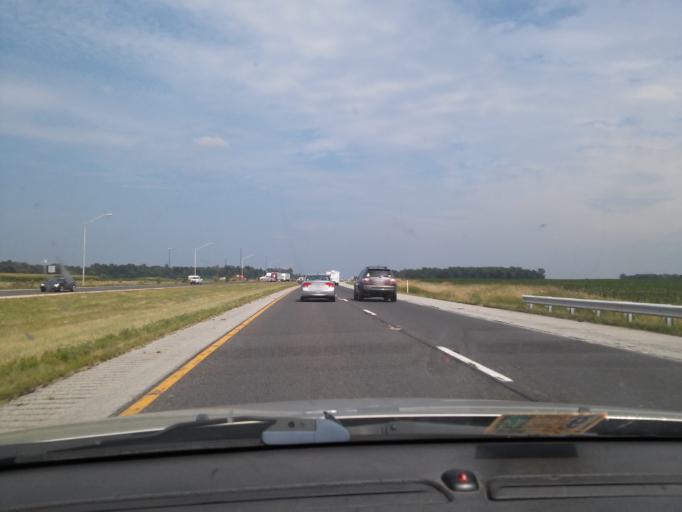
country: US
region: Indiana
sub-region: Wayne County
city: Centerville
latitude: 39.8593
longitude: -85.0359
